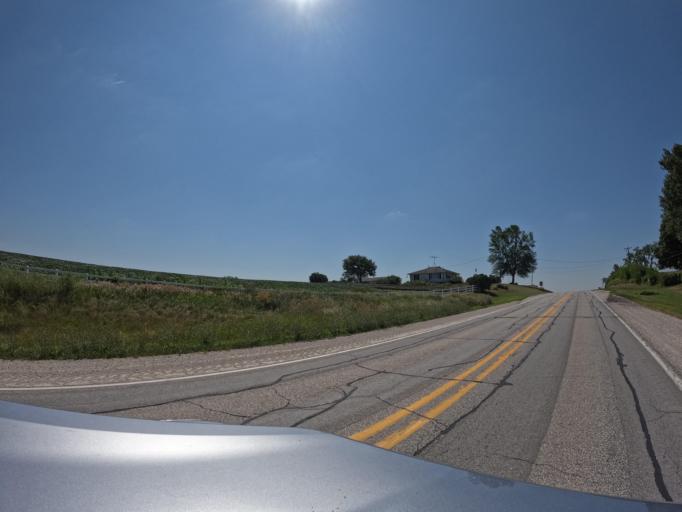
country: US
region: Iowa
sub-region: Keokuk County
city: Sigourney
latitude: 41.3198
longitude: -92.2052
